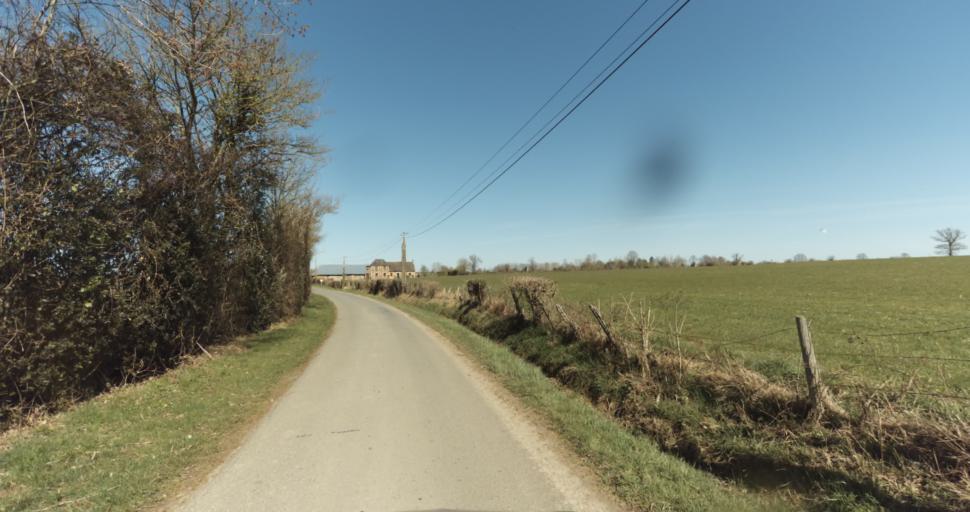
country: FR
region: Lower Normandy
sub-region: Departement du Calvados
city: Livarot
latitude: 49.0117
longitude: 0.1049
